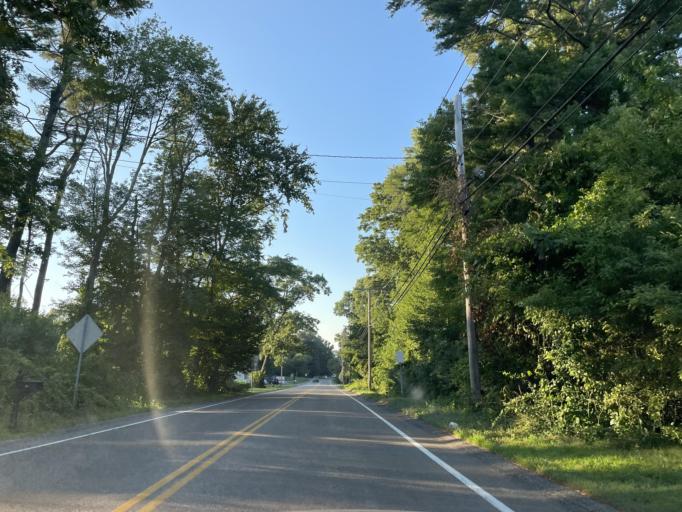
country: US
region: Massachusetts
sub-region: Plymouth County
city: Halifax
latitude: 41.9972
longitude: -70.8444
